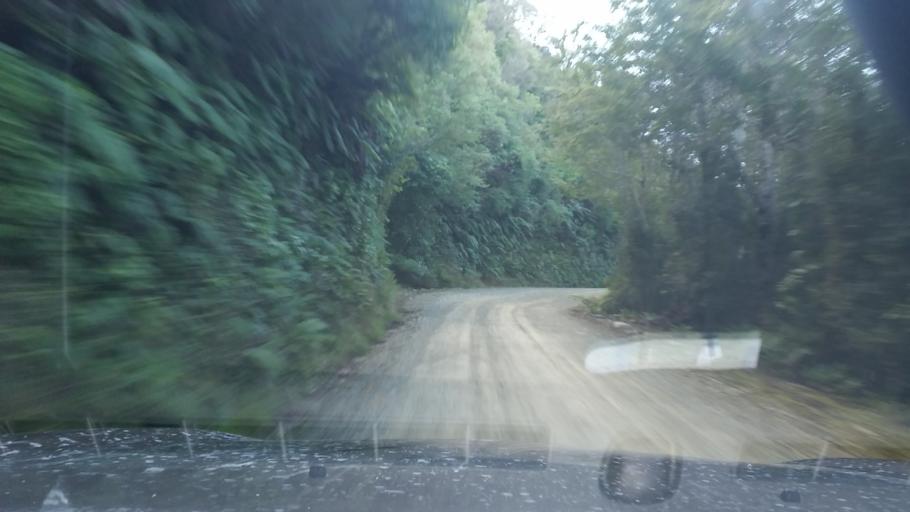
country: NZ
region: Marlborough
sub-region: Marlborough District
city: Picton
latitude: -41.0924
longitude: 174.1360
